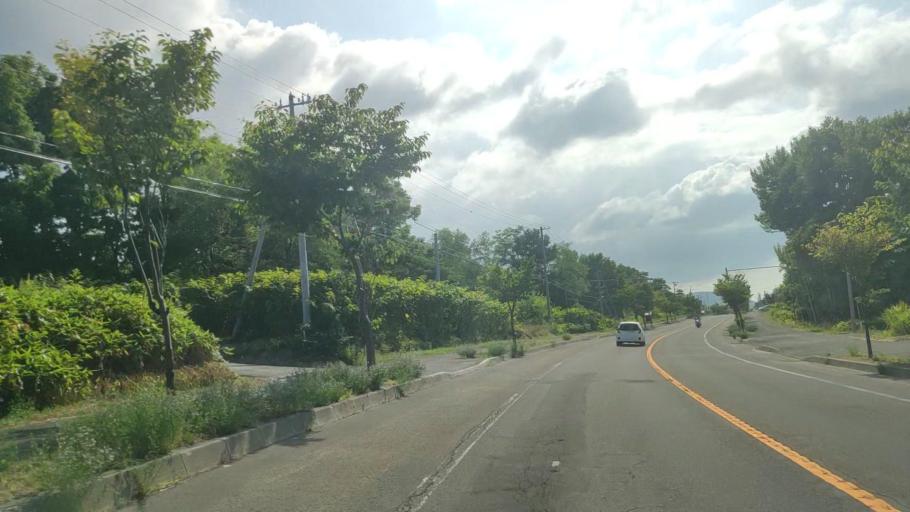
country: JP
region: Hokkaido
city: Rumoi
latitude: 43.8517
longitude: 141.5415
